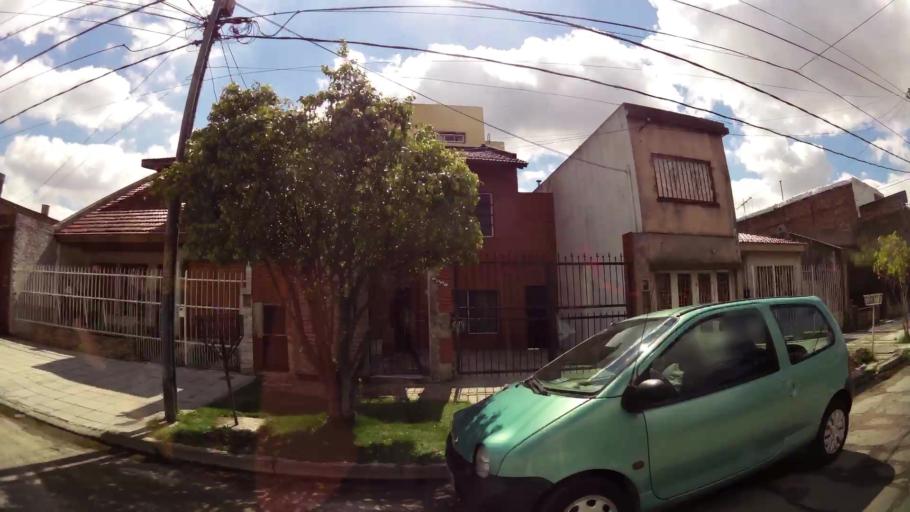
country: AR
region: Buenos Aires
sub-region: Partido de Lanus
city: Lanus
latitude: -34.6799
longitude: -58.4161
